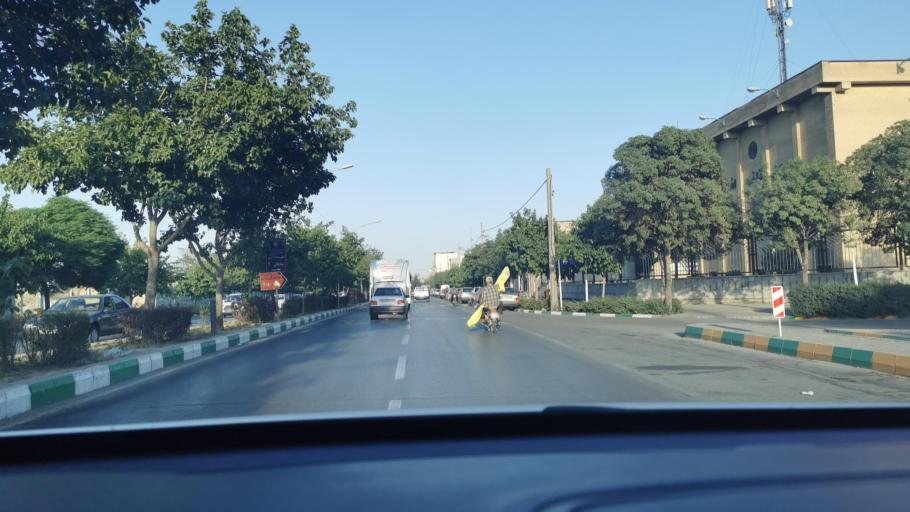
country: IR
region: Razavi Khorasan
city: Mashhad
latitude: 36.2892
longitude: 59.6534
